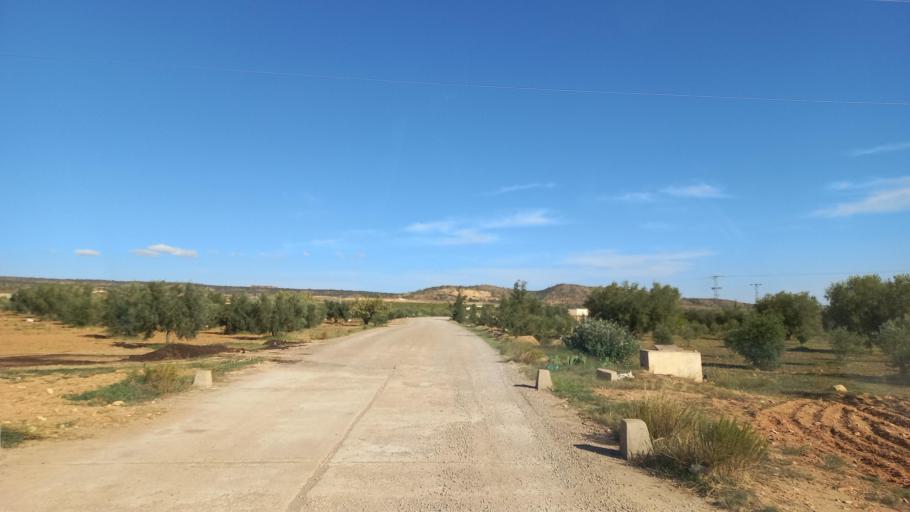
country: TN
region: Al Qasrayn
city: Sbiba
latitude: 35.2956
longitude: 9.1043
